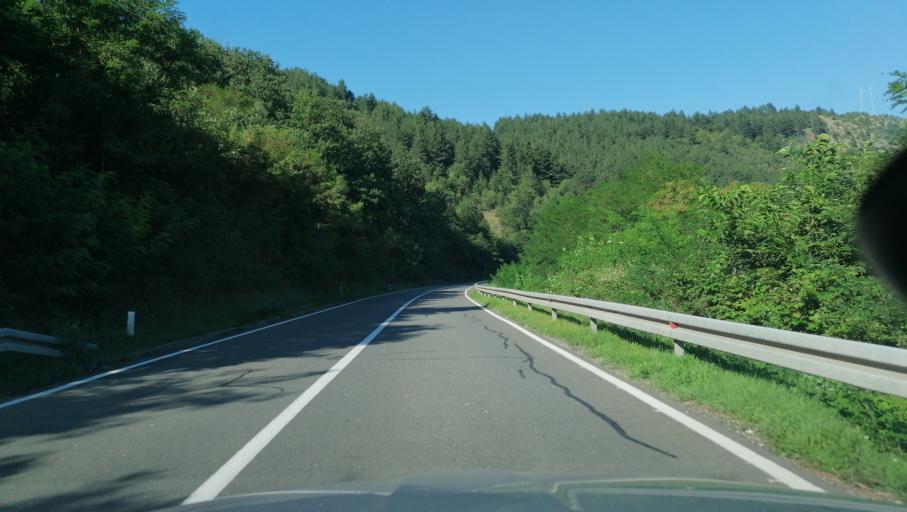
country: RS
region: Central Serbia
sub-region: Raski Okrug
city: Kraljevo
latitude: 43.6650
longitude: 20.5672
